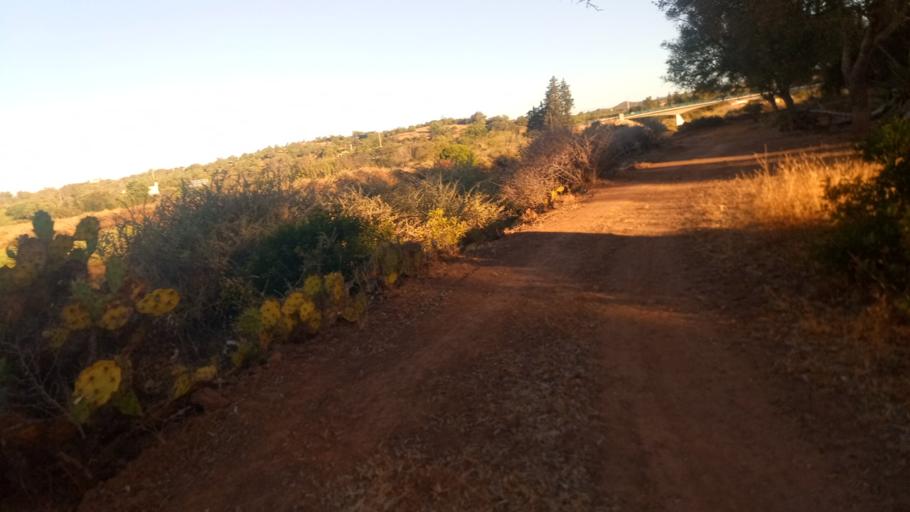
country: PT
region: Faro
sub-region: Tavira
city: Tavira
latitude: 37.1440
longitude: -7.6167
